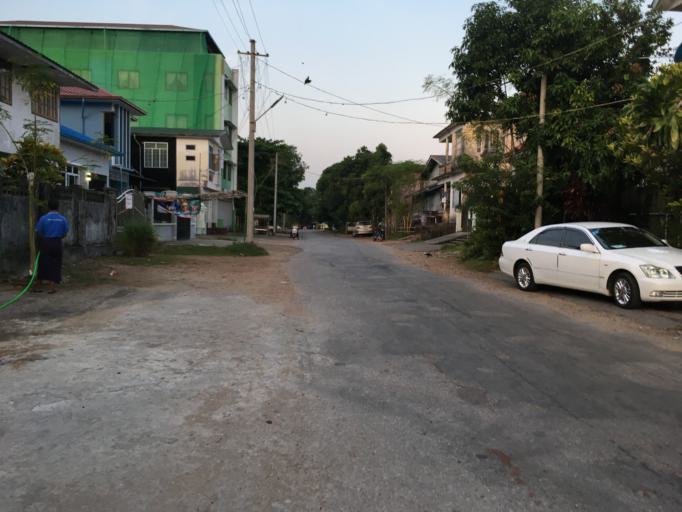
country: MM
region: Mon
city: Mawlamyine
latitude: 16.4780
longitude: 97.6232
